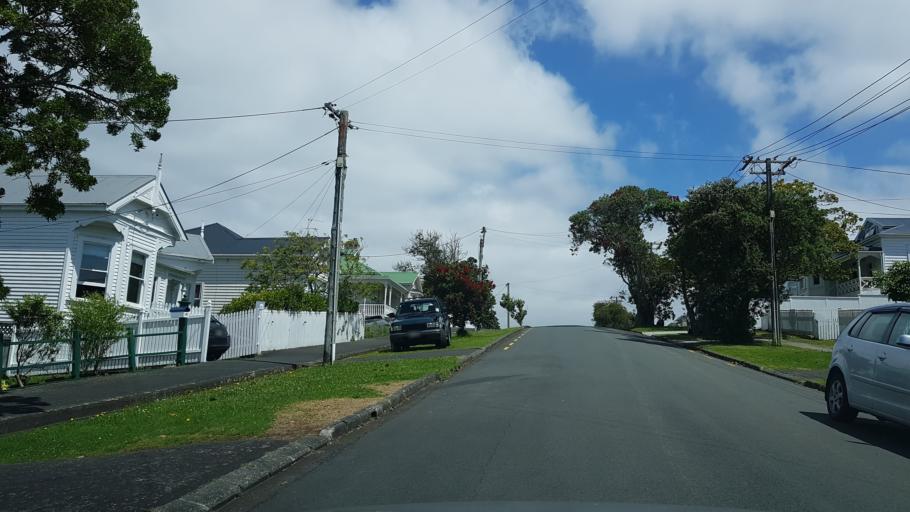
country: NZ
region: Auckland
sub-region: Auckland
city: North Shore
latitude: -36.8147
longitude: 174.7465
